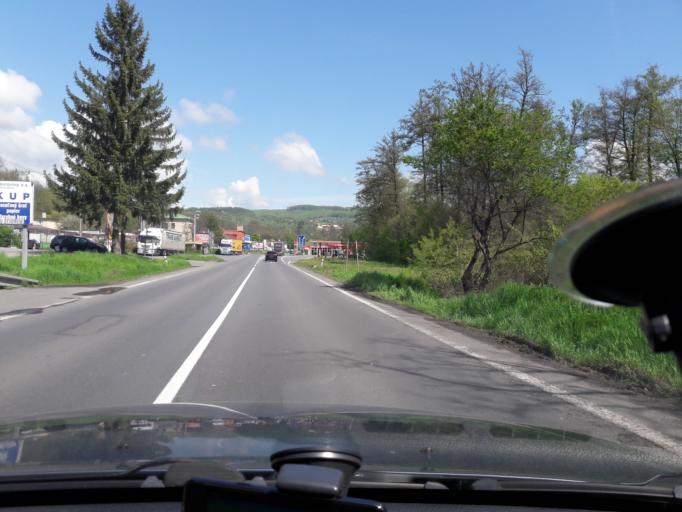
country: SK
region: Banskobystricky
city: Krupina
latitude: 48.3673
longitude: 19.0646
